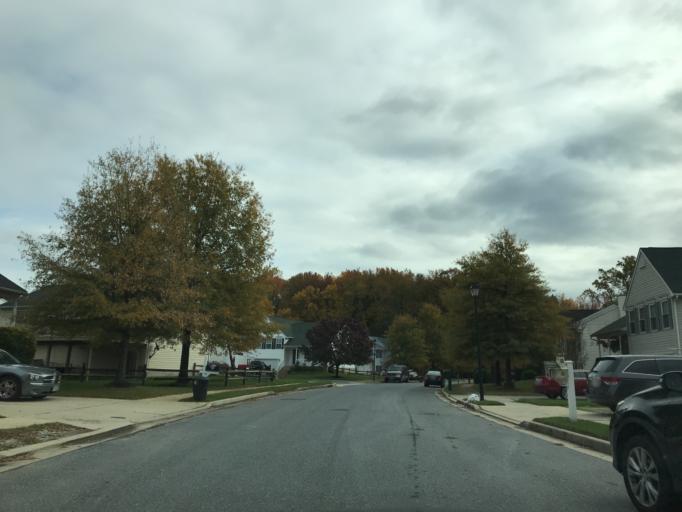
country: US
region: Maryland
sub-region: Baltimore County
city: Bowleys Quarters
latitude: 39.3248
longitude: -76.3913
